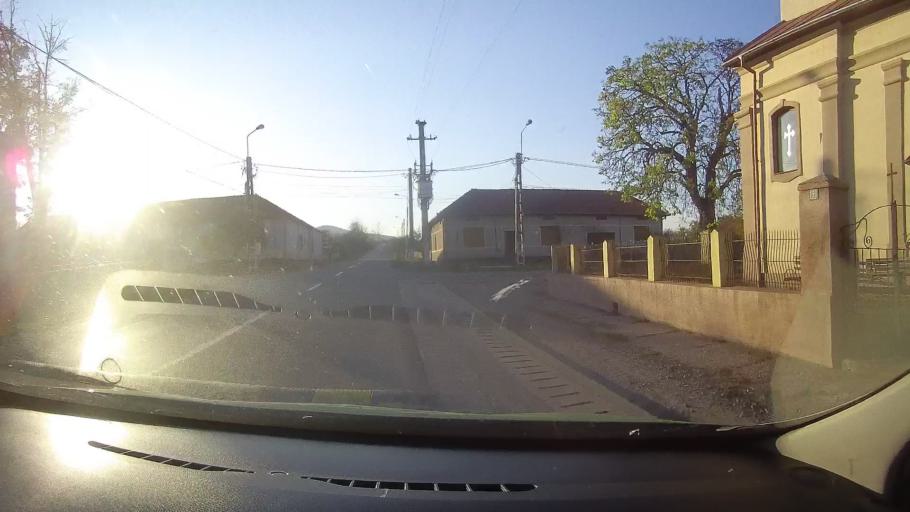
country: RO
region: Timis
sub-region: Comuna Fardea
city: Fardea
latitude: 45.7420
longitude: 22.1616
